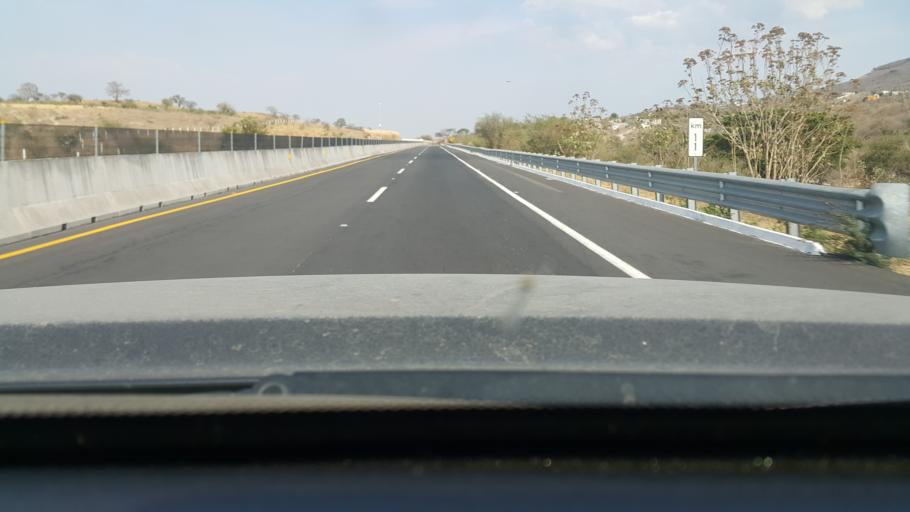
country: MX
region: Nayarit
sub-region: Ahuacatlan
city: Ahuacatlan
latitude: 21.0564
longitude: -104.5264
